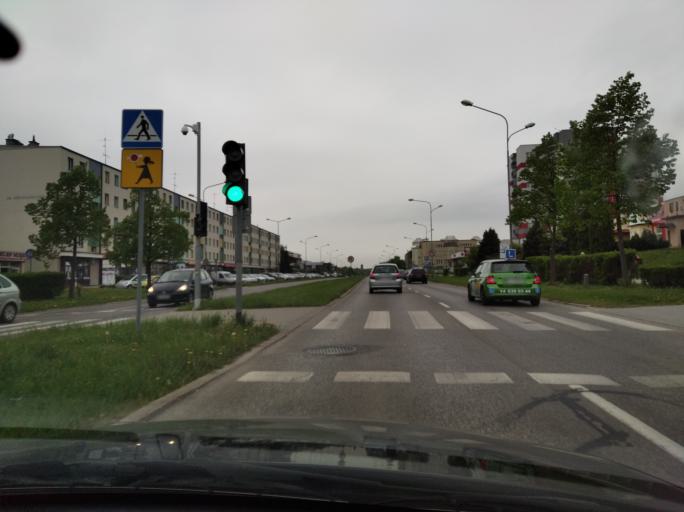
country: PL
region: Lesser Poland Voivodeship
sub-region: Powiat tarnowski
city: Tarnow
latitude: 50.0173
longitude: 21.0052
